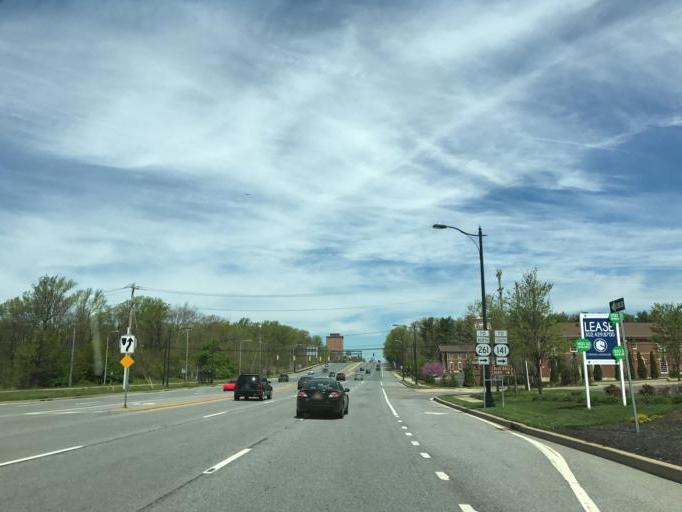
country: US
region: Delaware
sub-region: New Castle County
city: Wilmington
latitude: 39.7792
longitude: -75.5450
